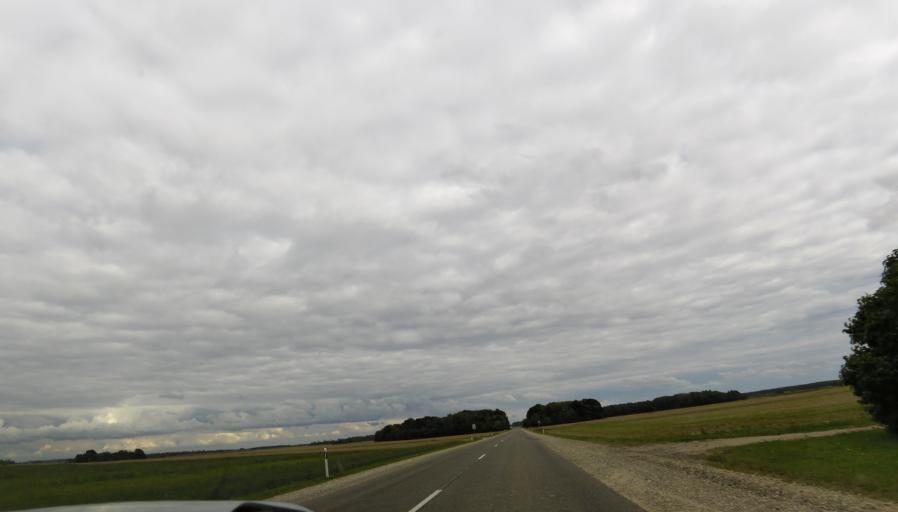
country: LT
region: Panevezys
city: Pasvalys
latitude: 56.0225
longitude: 24.2309
